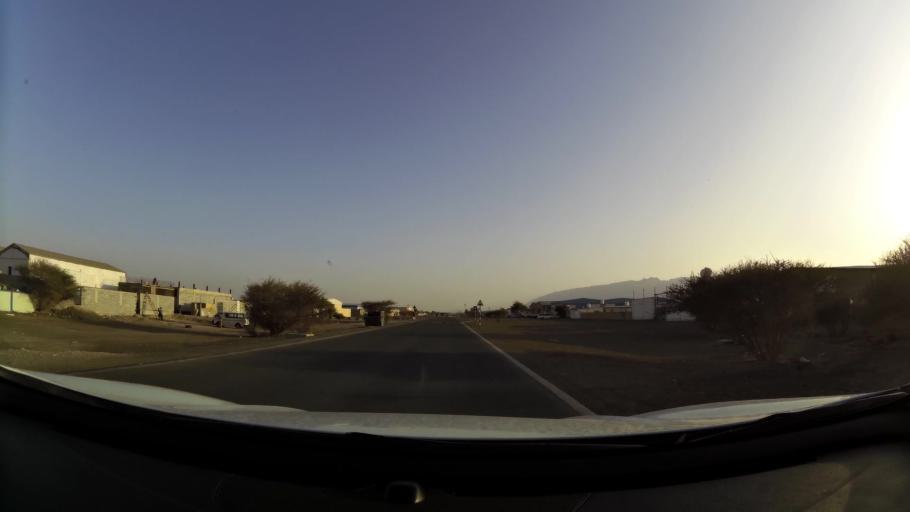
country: AE
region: Abu Dhabi
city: Al Ain
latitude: 24.1535
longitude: 55.8190
